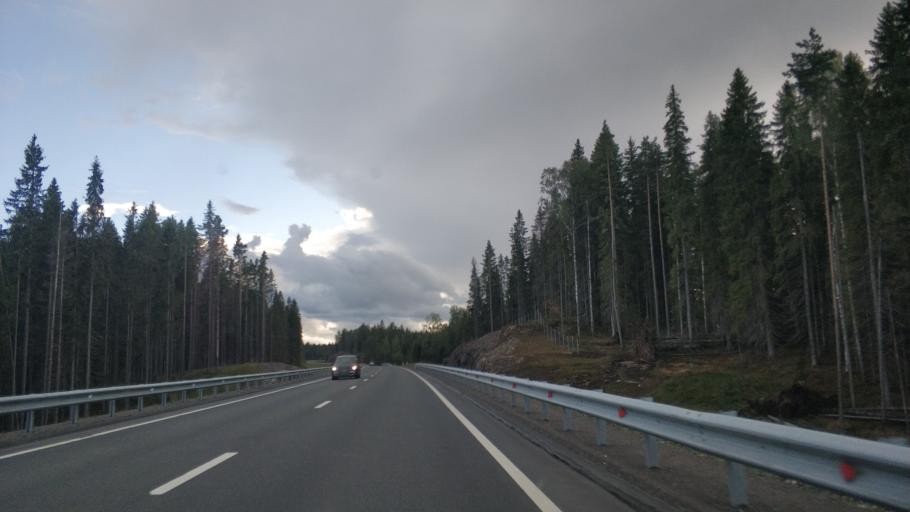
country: RU
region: Republic of Karelia
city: Lakhdenpokh'ya
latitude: 61.4292
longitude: 29.9703
